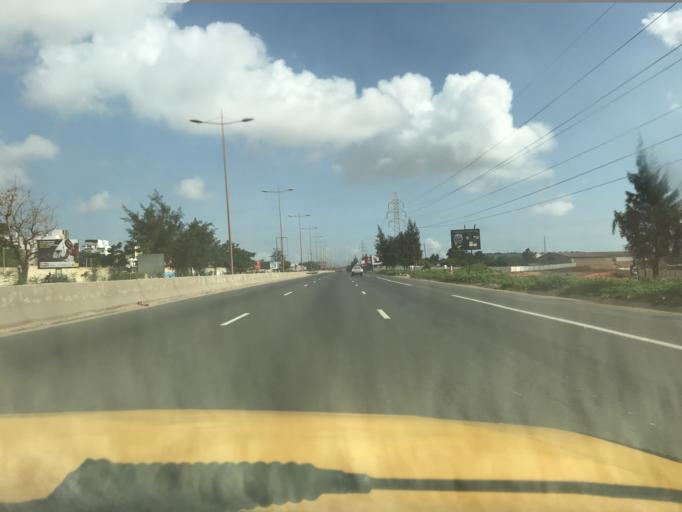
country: SN
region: Dakar
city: Grand Dakar
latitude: 14.7106
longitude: -17.4414
